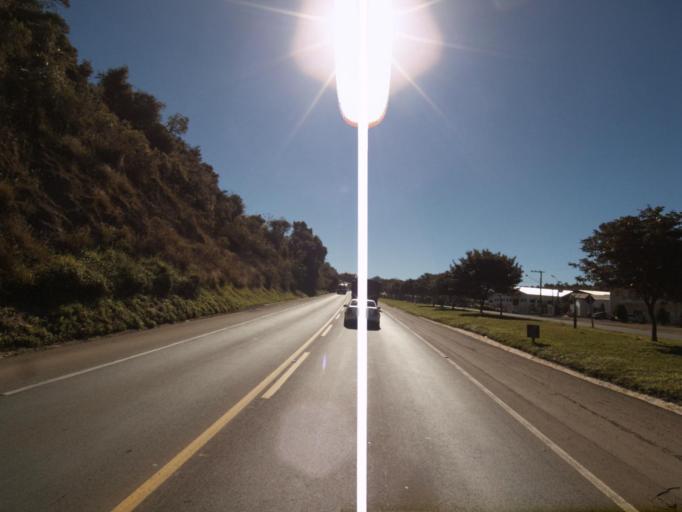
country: BR
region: Santa Catarina
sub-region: Chapeco
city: Chapeco
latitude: -26.9908
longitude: -52.6098
